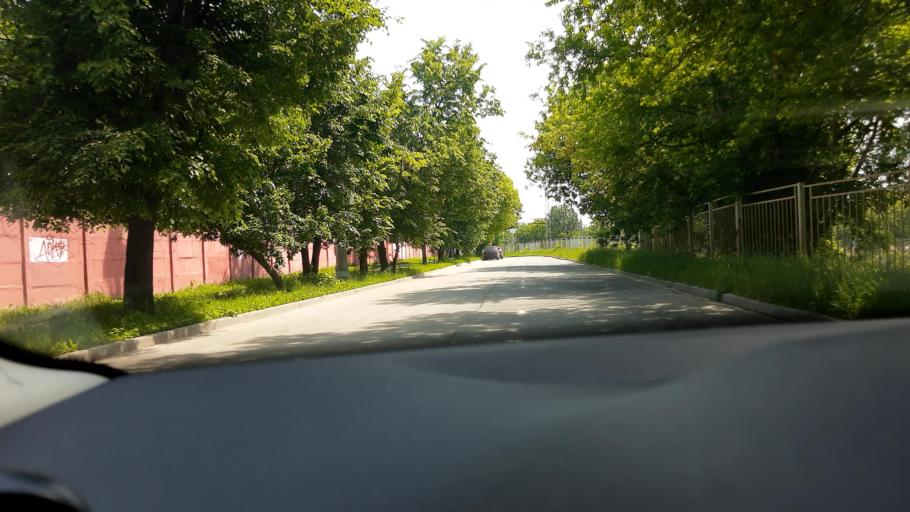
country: RU
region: Moscow
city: Strogino
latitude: 55.8292
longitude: 37.4317
